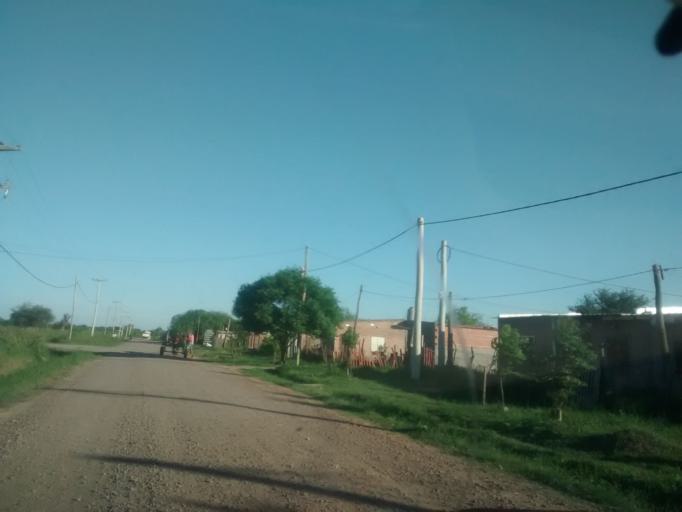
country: AR
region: Chaco
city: Fontana
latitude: -27.4618
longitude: -59.0319
